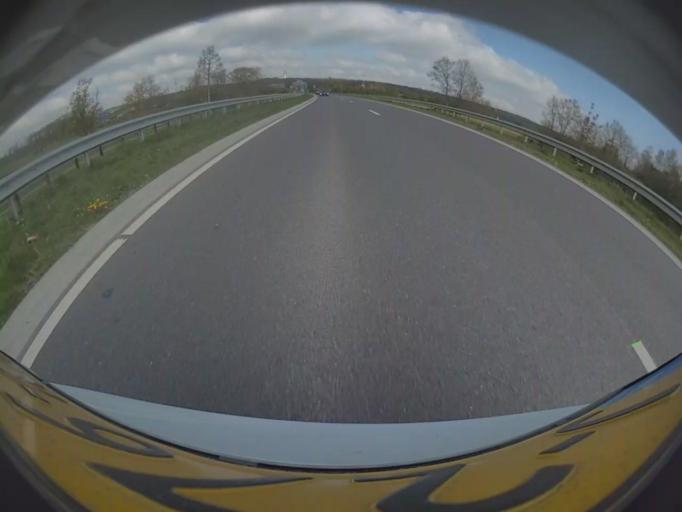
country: BE
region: Wallonia
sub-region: Province du Luxembourg
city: Marche-en-Famenne
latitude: 50.2305
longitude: 5.3126
